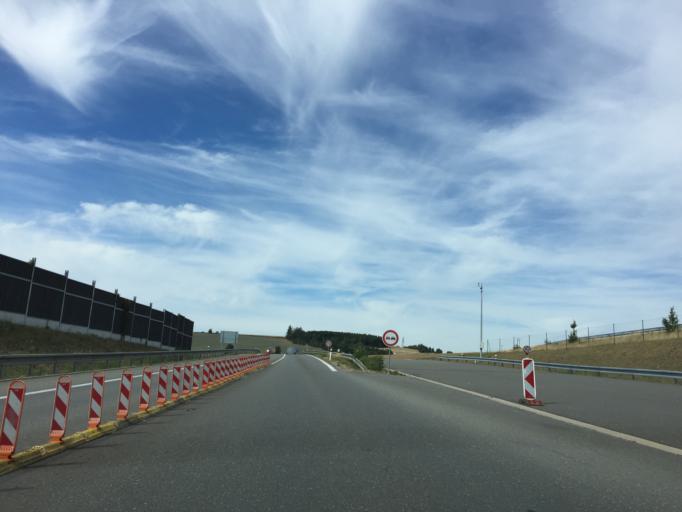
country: CZ
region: Jihocesky
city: Chotoviny
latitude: 49.5432
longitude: 14.6656
